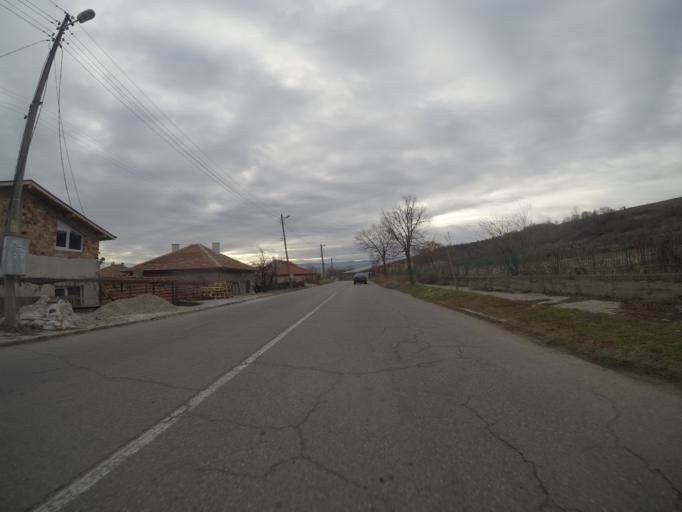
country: BG
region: Kyustendil
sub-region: Obshtina Kocherinovo
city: Kocherinovo
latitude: 42.0902
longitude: 23.0654
